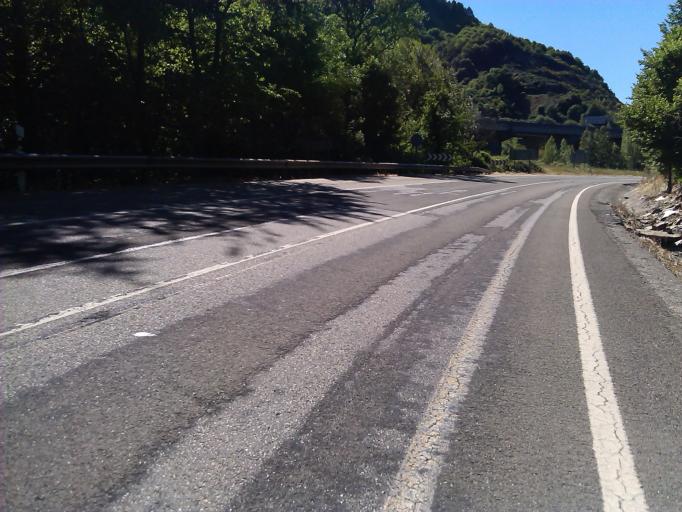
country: ES
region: Castille and Leon
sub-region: Provincia de Leon
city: Vega de Valcarce
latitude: 42.6609
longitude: -6.9243
